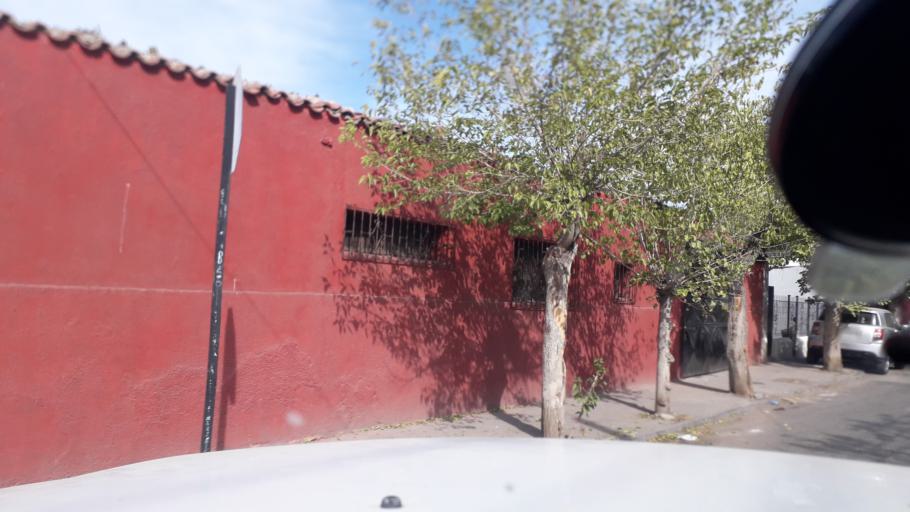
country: CL
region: Valparaiso
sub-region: Provincia de San Felipe
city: San Felipe
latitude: -32.7488
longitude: -70.7329
